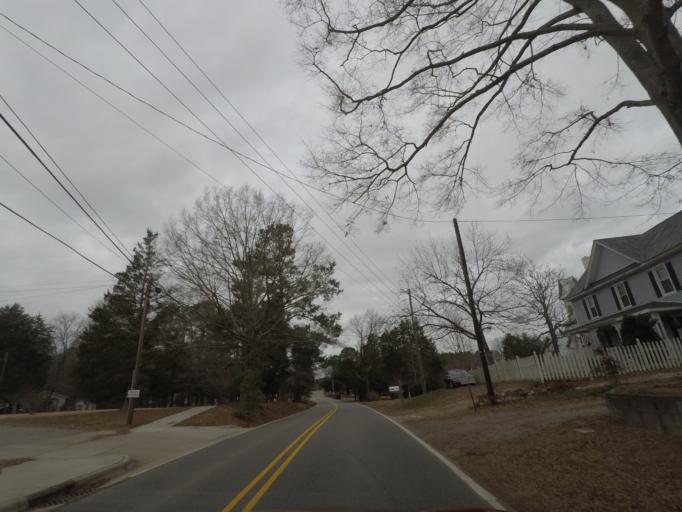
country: US
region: North Carolina
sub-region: Wake County
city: Morrisville
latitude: 35.8244
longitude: -78.8282
